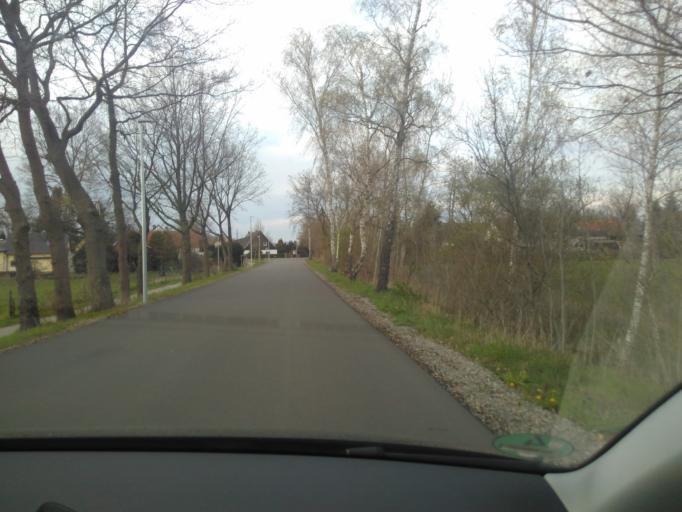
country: DE
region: Lower Saxony
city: Adelheidsdorf
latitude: 52.5510
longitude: 10.0311
